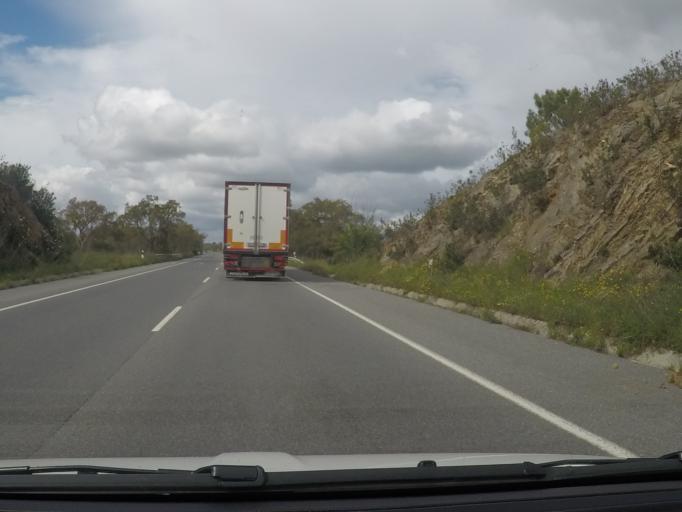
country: PT
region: Setubal
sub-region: Grandola
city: Grandola
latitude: 38.1489
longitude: -8.6498
